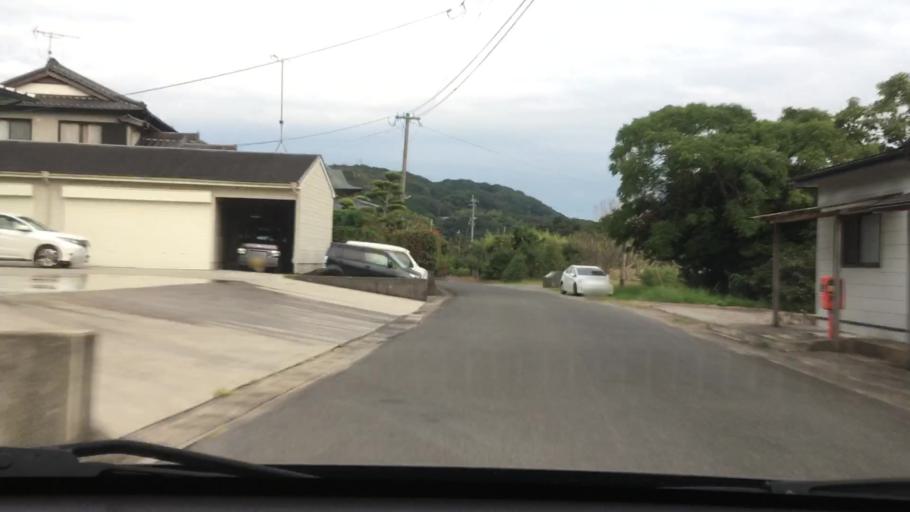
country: JP
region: Nagasaki
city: Sasebo
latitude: 33.0006
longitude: 129.7660
